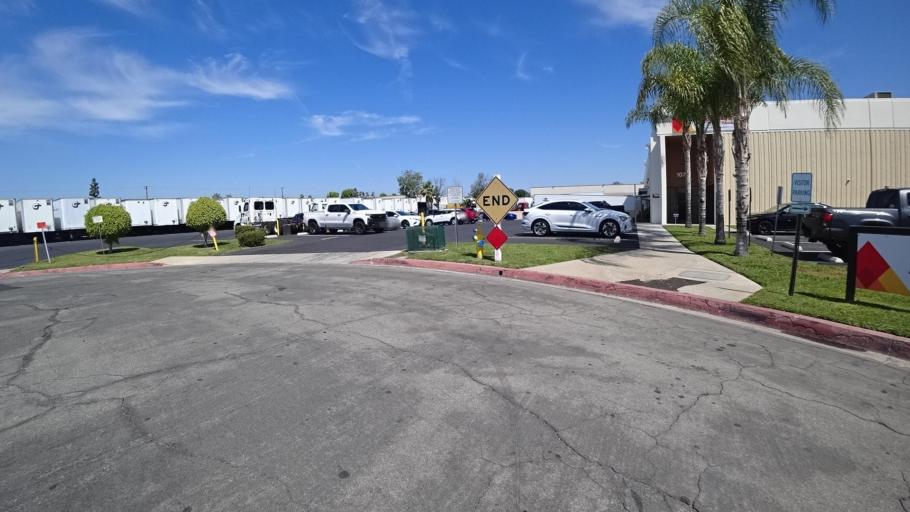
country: US
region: California
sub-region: Los Angeles County
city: South San Jose Hills
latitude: 33.9991
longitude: -117.9098
